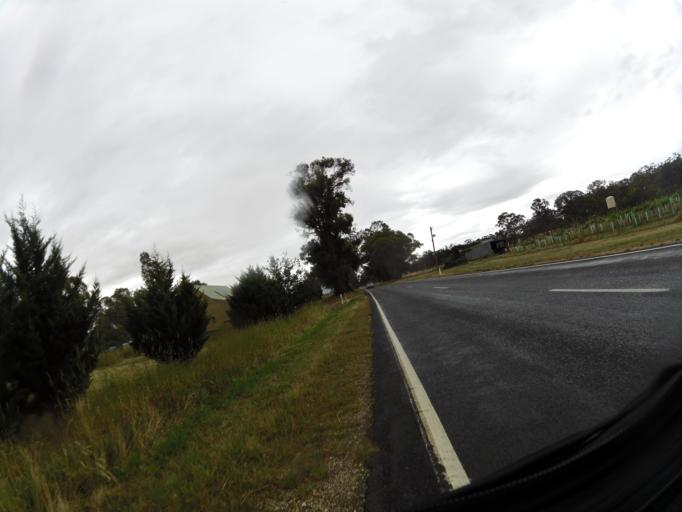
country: AU
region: Victoria
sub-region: Mount Alexander
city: Castlemaine
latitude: -37.1427
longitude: 144.0411
